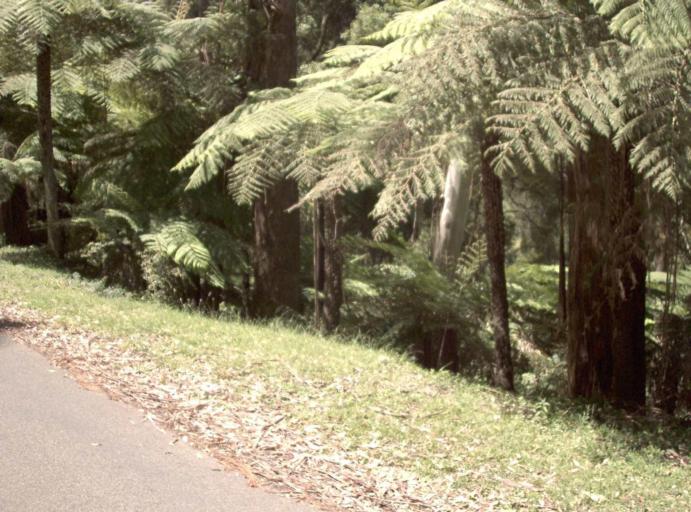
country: AU
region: Victoria
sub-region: Yarra Ranges
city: Millgrove
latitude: -37.7425
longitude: 145.7122
